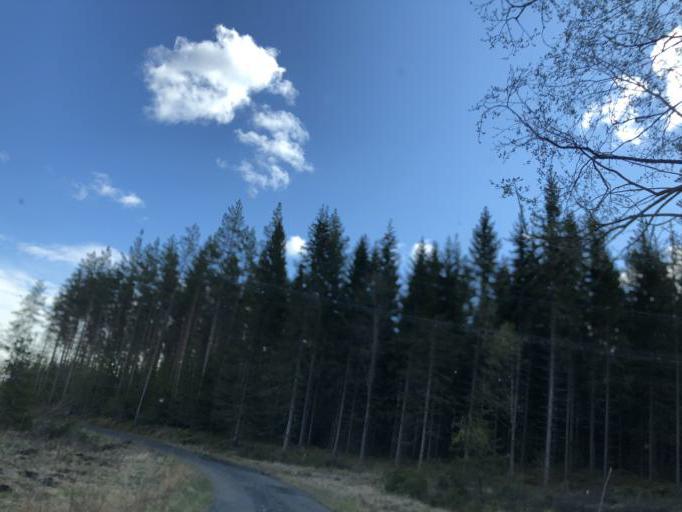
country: SE
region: Uppsala
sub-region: Heby Kommun
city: Tarnsjo
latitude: 60.2322
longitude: 16.7150
